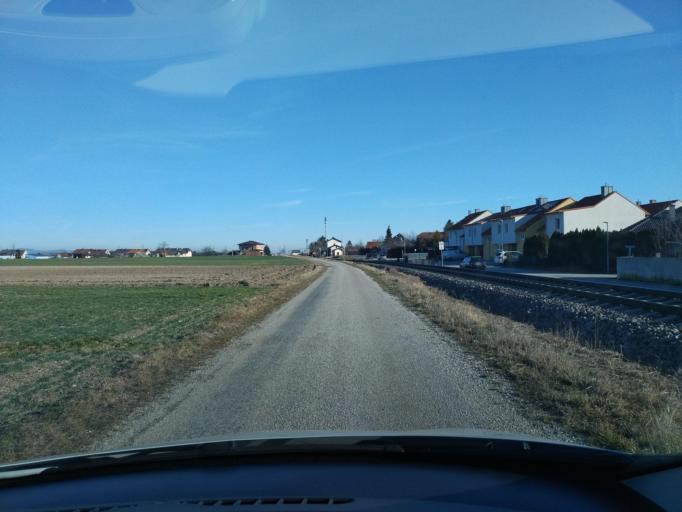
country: AT
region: Lower Austria
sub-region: Politischer Bezirk Wiener Neustadt
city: Lanzenkirchen
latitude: 47.7480
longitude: 16.2415
